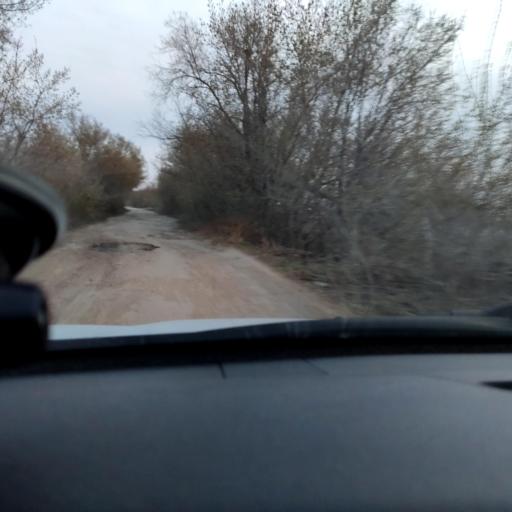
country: RU
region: Samara
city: Smyshlyayevka
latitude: 53.1544
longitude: 50.3925
